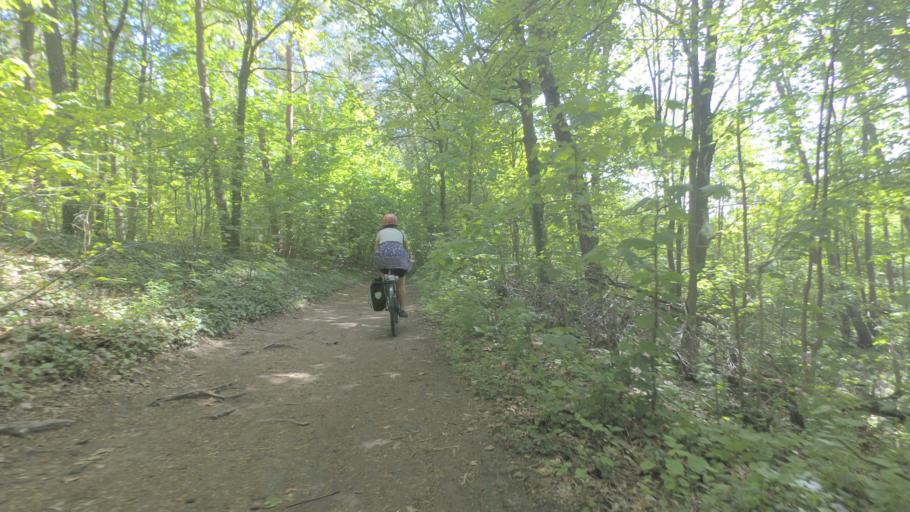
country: DE
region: Brandenburg
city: Erkner
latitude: 52.4244
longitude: 13.7638
